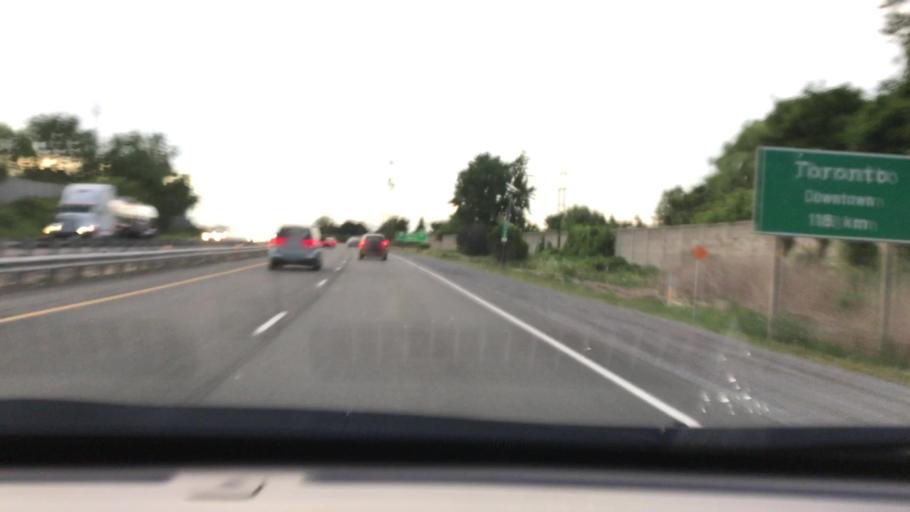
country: CA
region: Ontario
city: Niagara Falls
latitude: 43.1254
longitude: -79.1223
